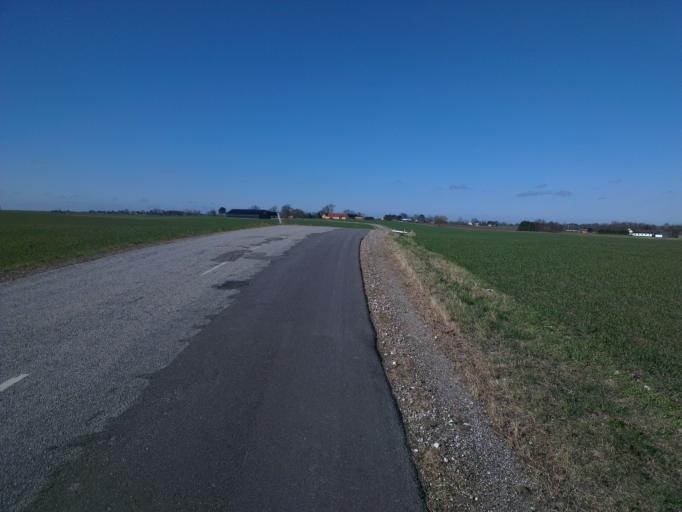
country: DK
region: Capital Region
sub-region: Hillerod Kommune
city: Skaevinge
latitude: 55.8808
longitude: 12.1075
